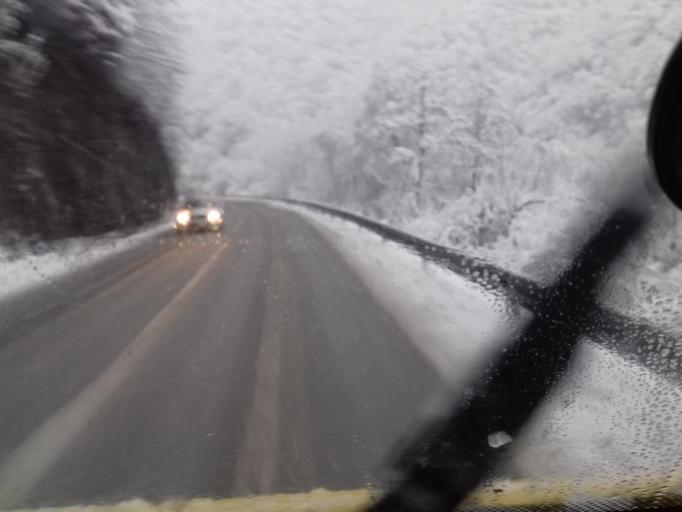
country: BA
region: Federation of Bosnia and Herzegovina
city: Busovaca
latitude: 44.1341
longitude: 17.9158
